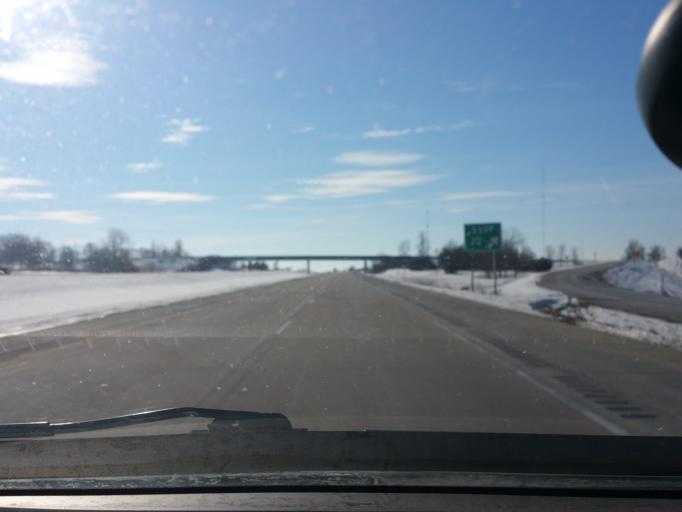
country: US
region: Iowa
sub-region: Decatur County
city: Leon
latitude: 40.8734
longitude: -93.8024
